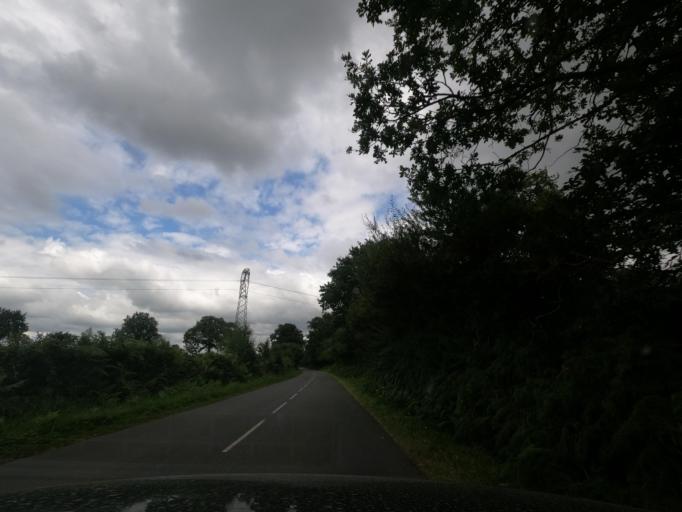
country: FR
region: Lower Normandy
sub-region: Departement de l'Orne
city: Briouze
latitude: 48.7175
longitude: -0.3588
